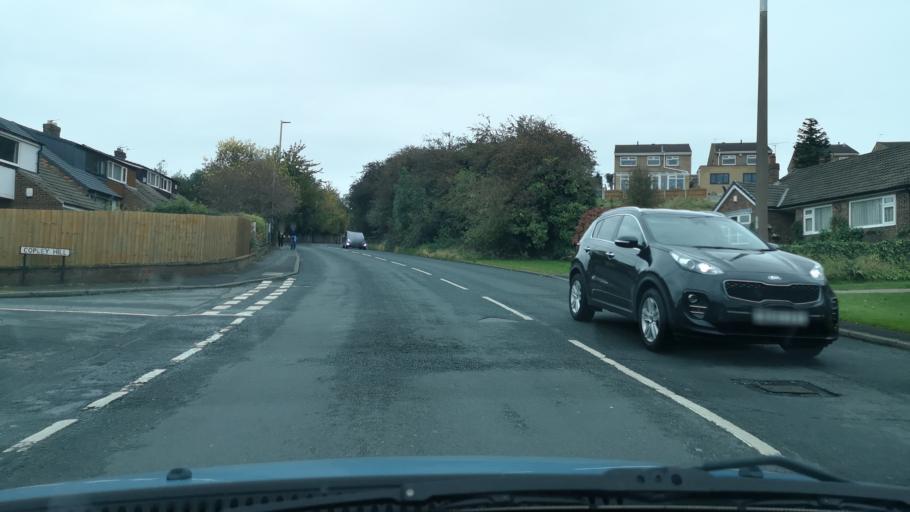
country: GB
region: England
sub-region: City and Borough of Leeds
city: Drighlington
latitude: 53.7328
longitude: -1.6539
